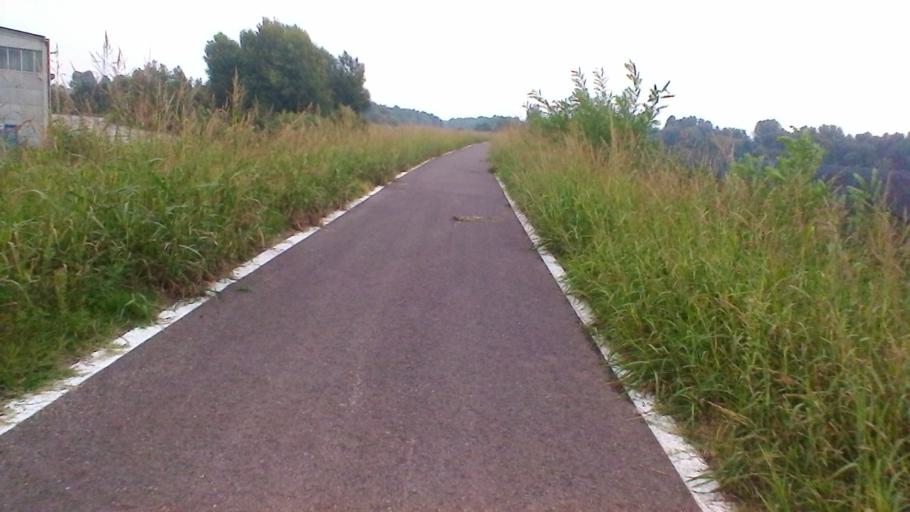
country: IT
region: Veneto
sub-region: Provincia di Verona
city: Zevio
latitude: 45.3836
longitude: 11.1291
